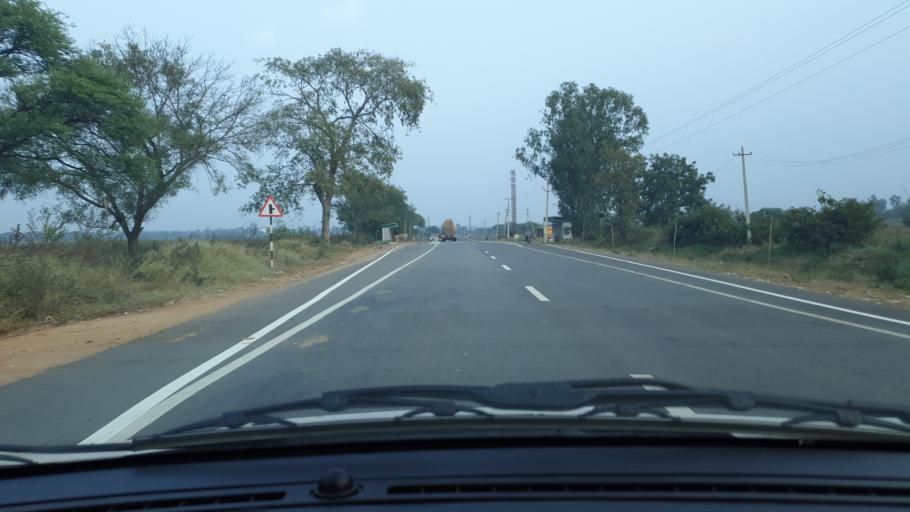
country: IN
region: Telangana
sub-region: Rangareddi
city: Vikarabad
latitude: 17.1651
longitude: 77.8280
